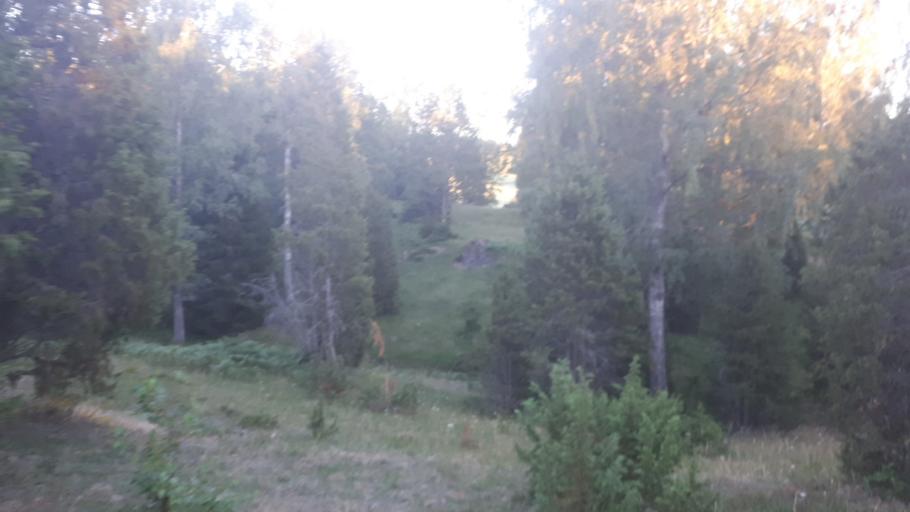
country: SE
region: Soedermanland
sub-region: Flens Kommun
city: Halleforsnas
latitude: 59.0724
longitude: 16.3834
